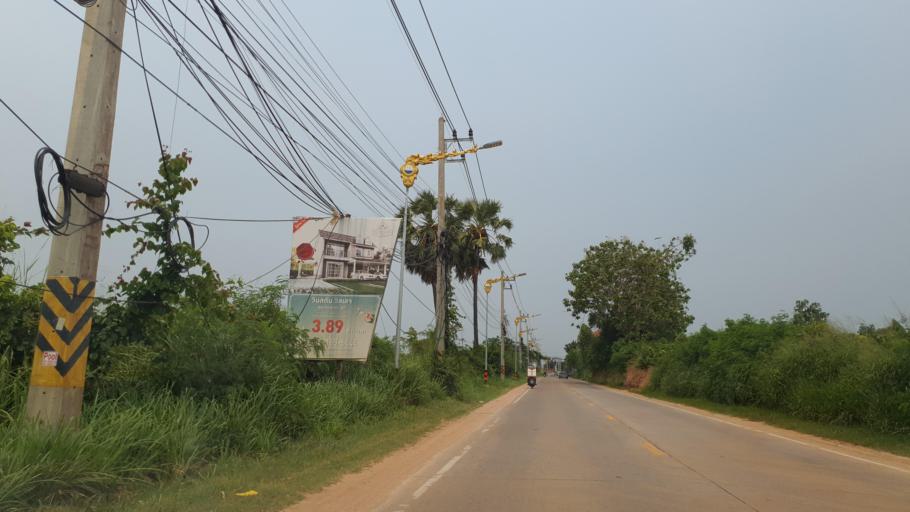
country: TH
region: Chon Buri
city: Phatthaya
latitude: 12.8966
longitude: 100.9186
